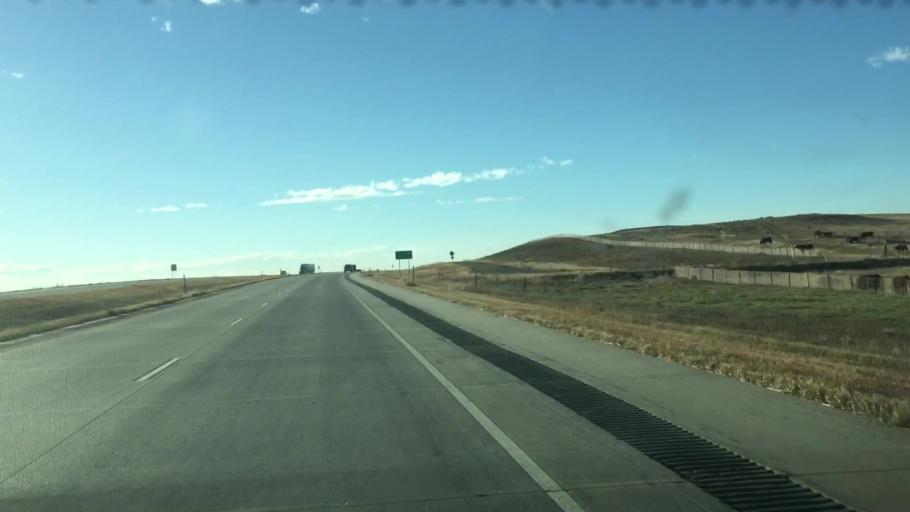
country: US
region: Colorado
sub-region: Lincoln County
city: Limon
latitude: 39.2859
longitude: -103.7843
